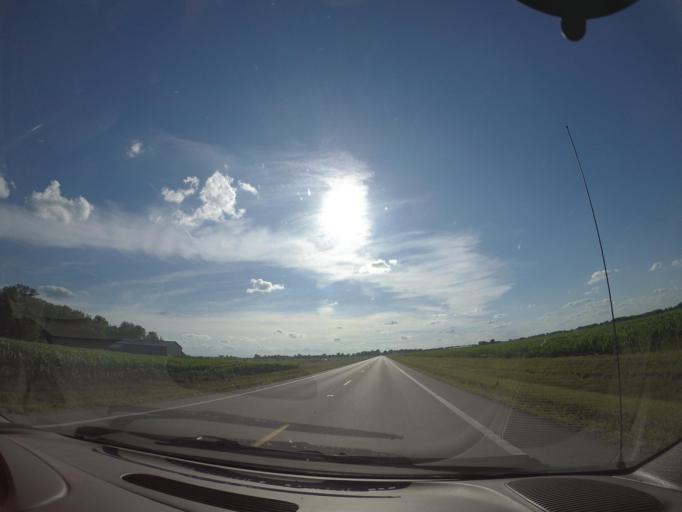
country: US
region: Ohio
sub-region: Henry County
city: Napoleon
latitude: 41.4323
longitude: -84.2226
